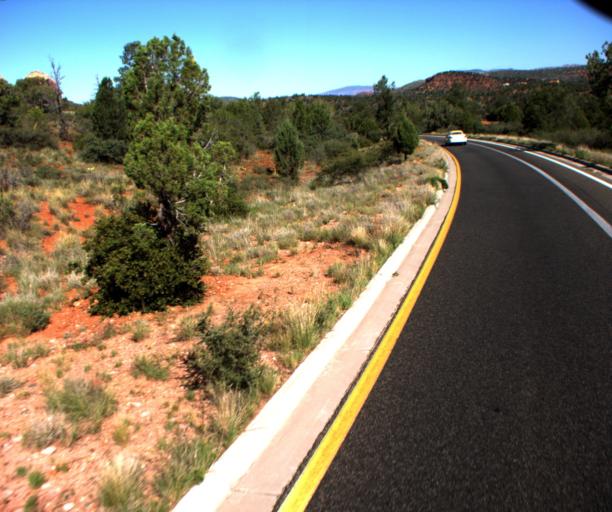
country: US
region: Arizona
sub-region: Yavapai County
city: Village of Oak Creek (Big Park)
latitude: 34.8165
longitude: -111.7672
